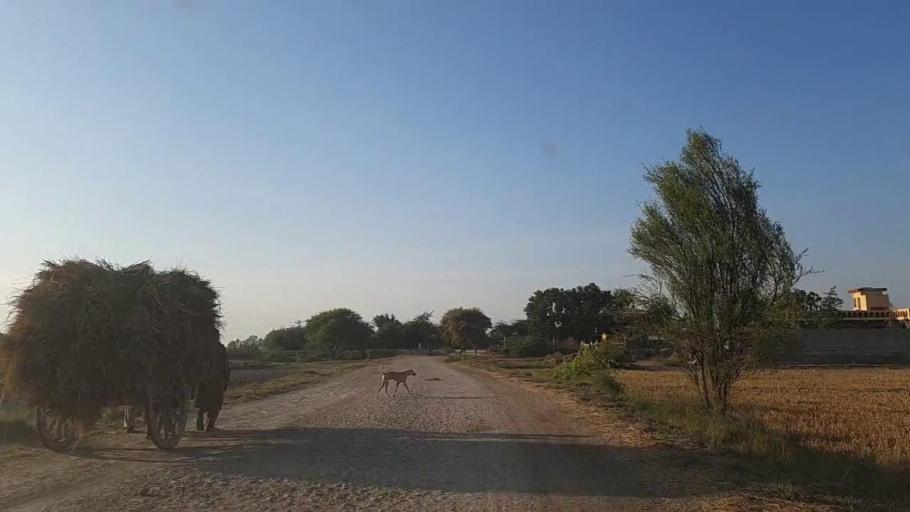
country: PK
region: Sindh
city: Mirpur Batoro
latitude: 24.6796
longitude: 68.2182
